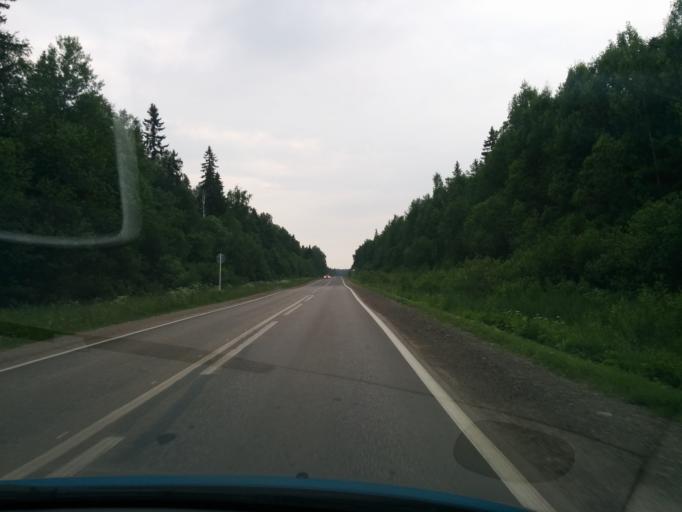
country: RU
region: Perm
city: Perm
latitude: 58.1834
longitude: 56.2224
